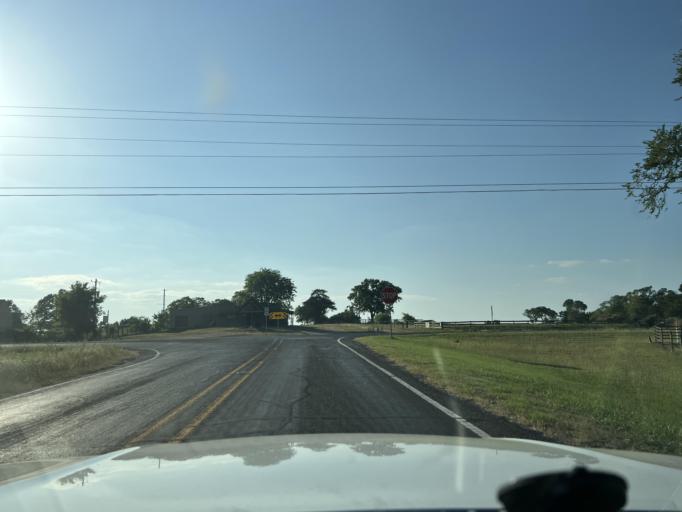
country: US
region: Texas
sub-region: Washington County
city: Brenham
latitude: 30.2354
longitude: -96.2850
